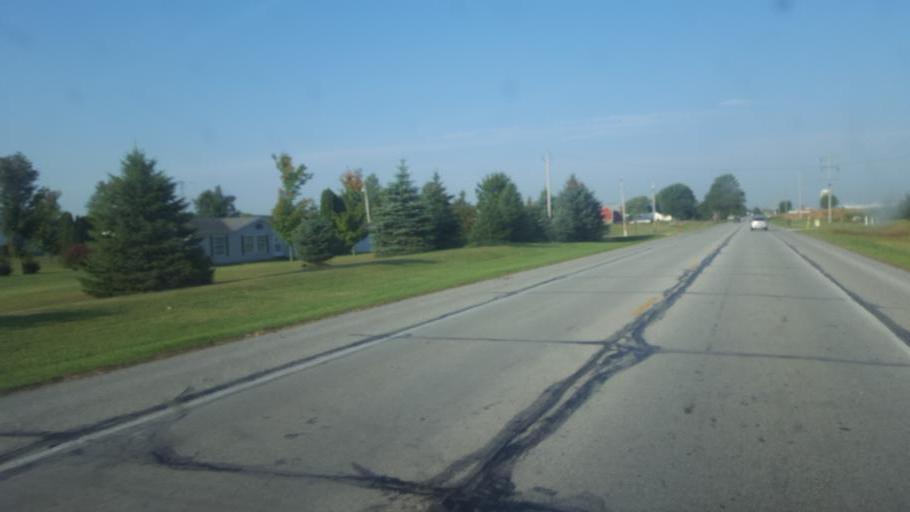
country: US
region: Indiana
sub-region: LaGrange County
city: Topeka
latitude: 41.6406
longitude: -85.5204
